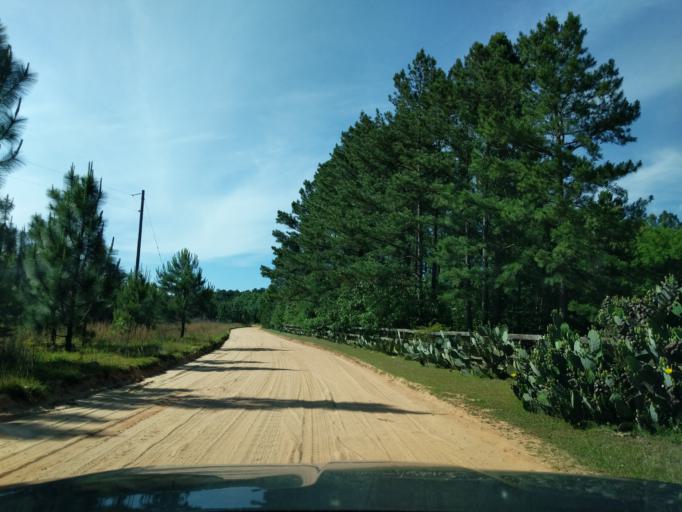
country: US
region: Georgia
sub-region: Jefferson County
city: Wrens
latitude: 33.2263
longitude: -82.3502
